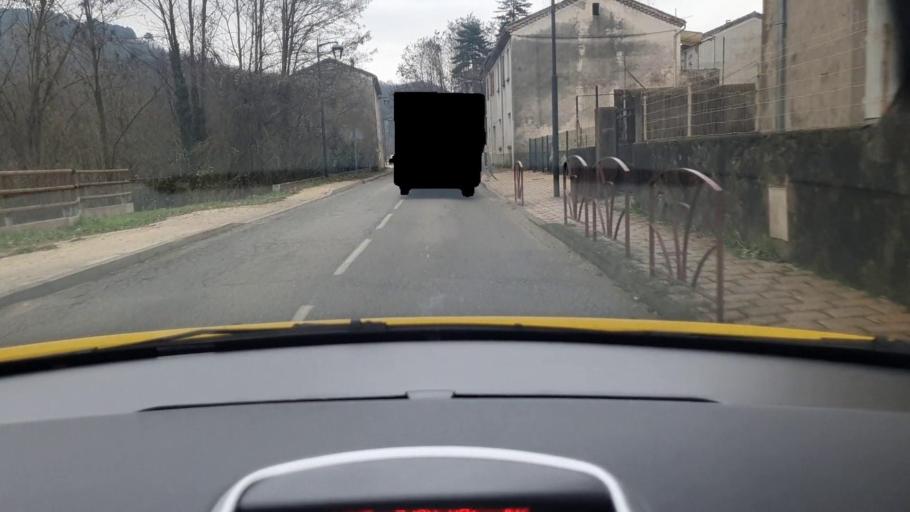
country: FR
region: Languedoc-Roussillon
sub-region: Departement du Gard
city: Besseges
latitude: 44.2818
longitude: 4.1187
